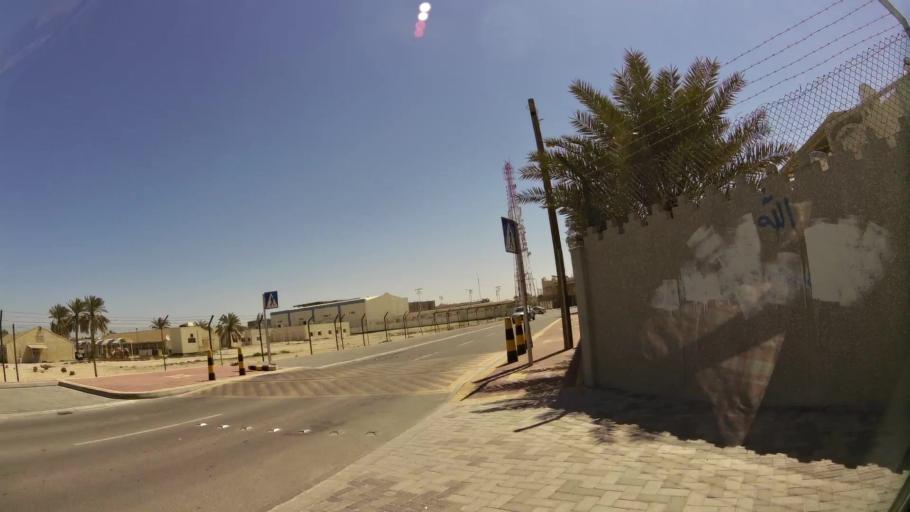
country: BH
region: Muharraq
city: Al Muharraq
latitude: 26.2692
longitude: 50.6128
